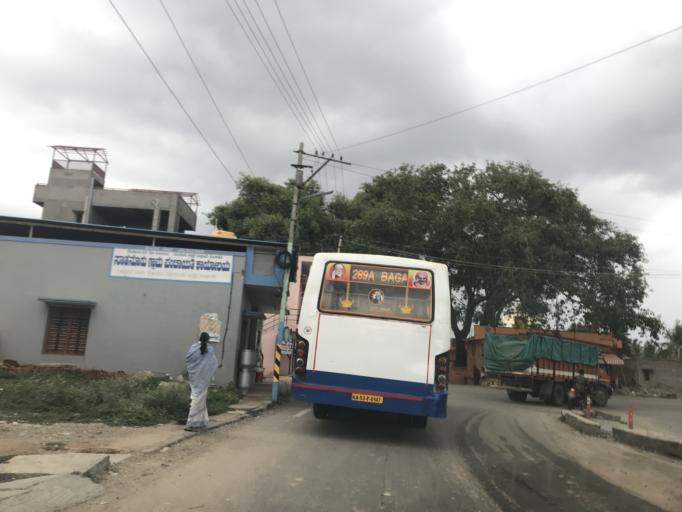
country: IN
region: Karnataka
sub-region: Bangalore Urban
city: Yelahanka
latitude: 13.1315
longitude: 77.6473
